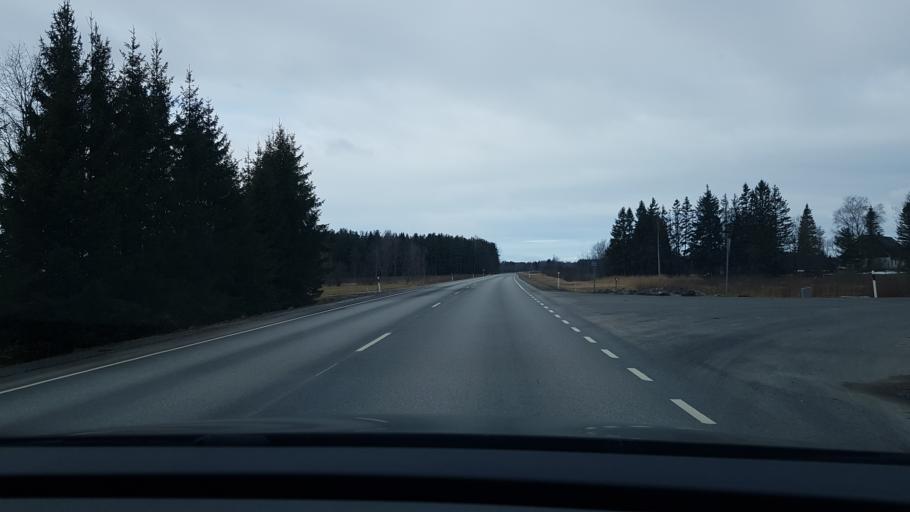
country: EE
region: Paernumaa
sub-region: Paikuse vald
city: Paikuse
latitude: 58.2683
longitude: 24.6425
